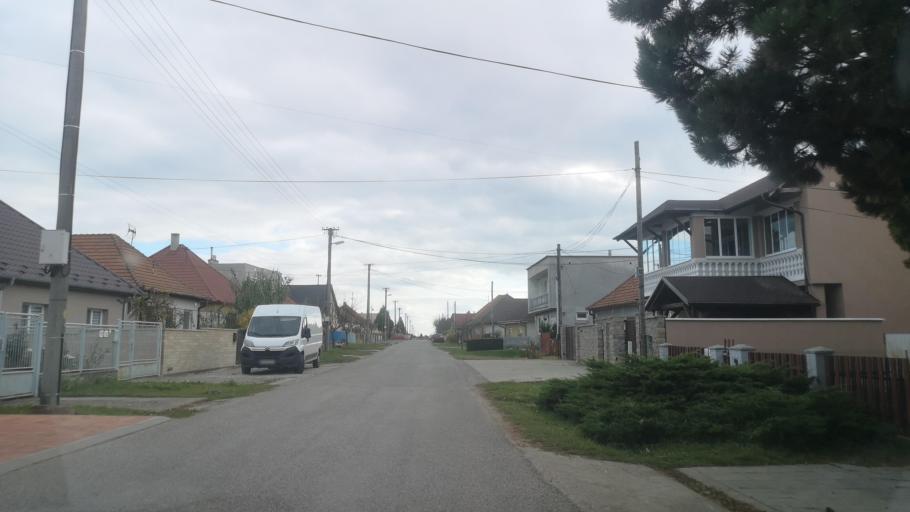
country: SK
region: Nitriansky
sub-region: Okres Nitra
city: Nitra
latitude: 48.3121
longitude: 17.9432
